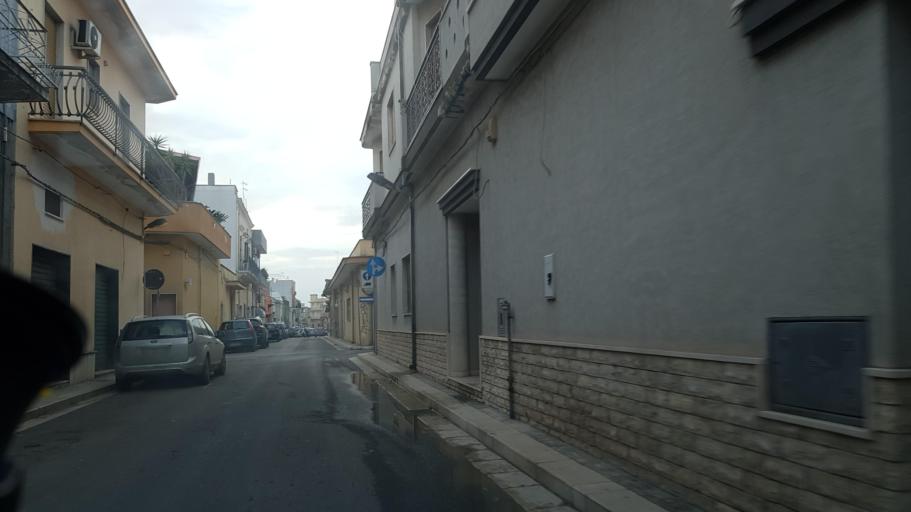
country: IT
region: Apulia
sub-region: Provincia di Brindisi
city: Mesagne
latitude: 40.5561
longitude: 17.8055
